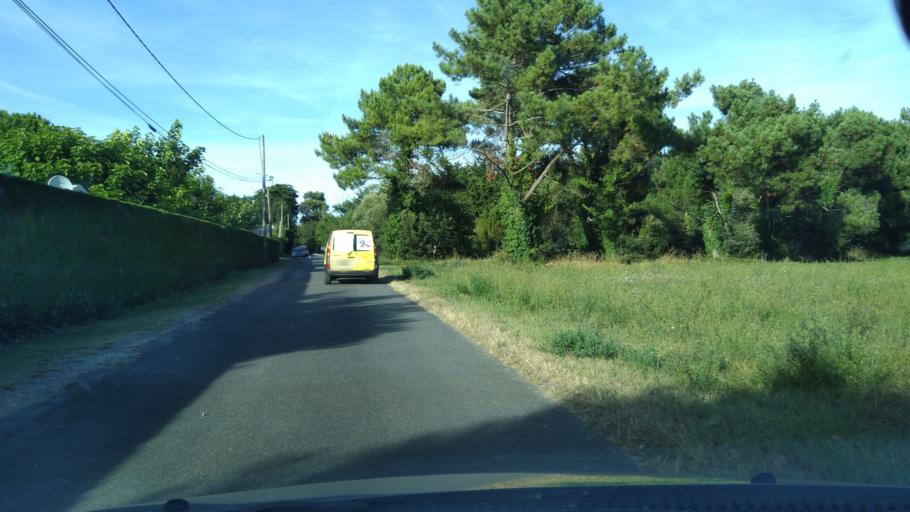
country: FR
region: Poitou-Charentes
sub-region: Departement de la Charente-Maritime
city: Saint-Denis-d'Oleron
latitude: 45.9568
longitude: -1.3627
